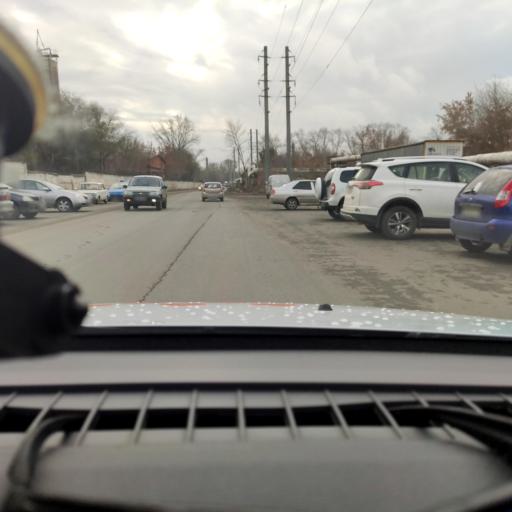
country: RU
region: Samara
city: Chapayevsk
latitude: 52.9758
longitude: 49.7156
